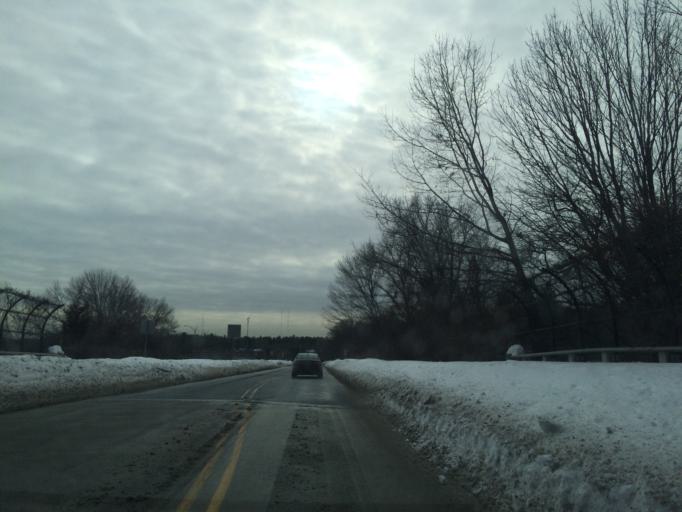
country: US
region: Massachusetts
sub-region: Middlesex County
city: Weston
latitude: 42.3403
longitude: -71.2702
